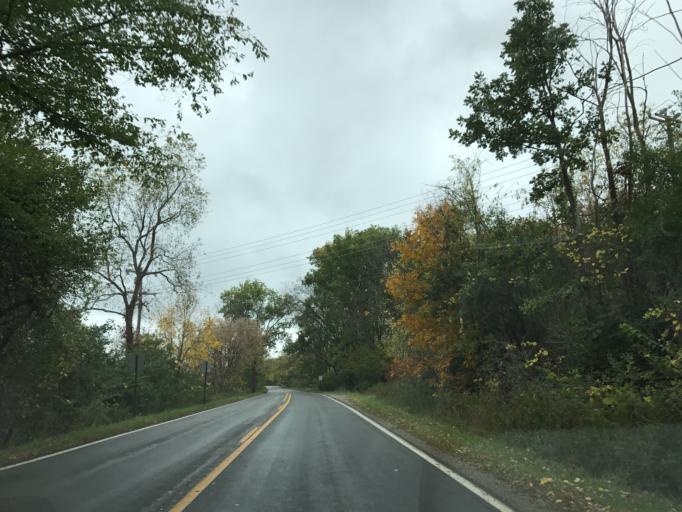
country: US
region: Michigan
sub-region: Washtenaw County
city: Ann Arbor
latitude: 42.2961
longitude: -83.6683
